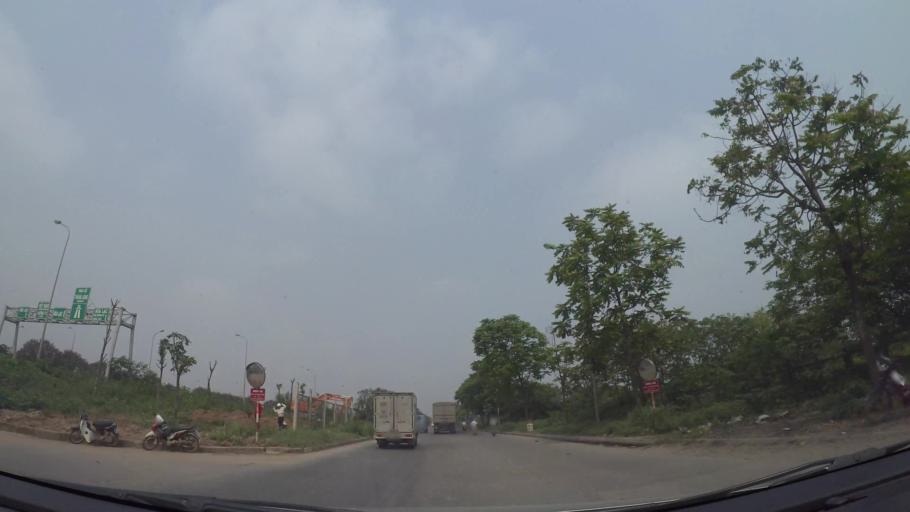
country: VN
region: Ha Noi
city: Cau Dien
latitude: 21.0089
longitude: 105.7533
